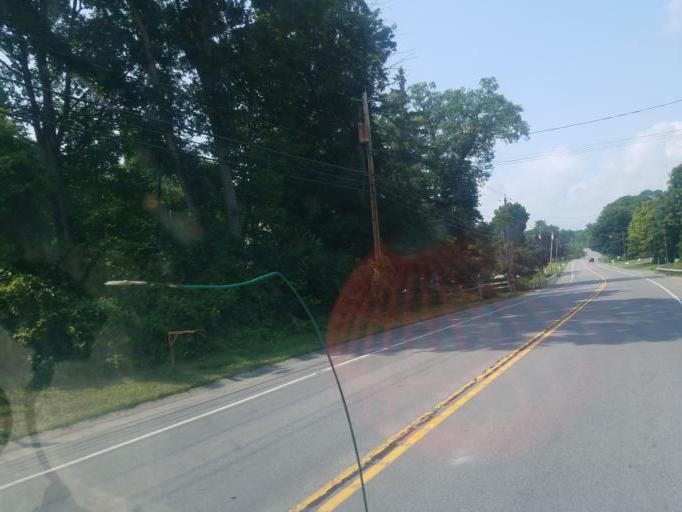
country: US
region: New York
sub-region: Montgomery County
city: Fonda
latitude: 42.9650
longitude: -74.3875
